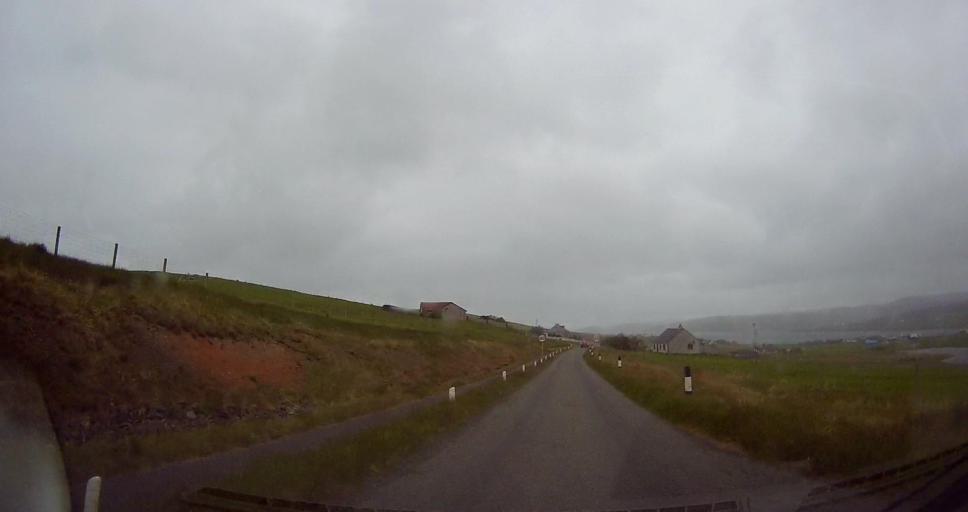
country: GB
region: Scotland
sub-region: Shetland Islands
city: Lerwick
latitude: 60.2775
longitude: -1.3896
